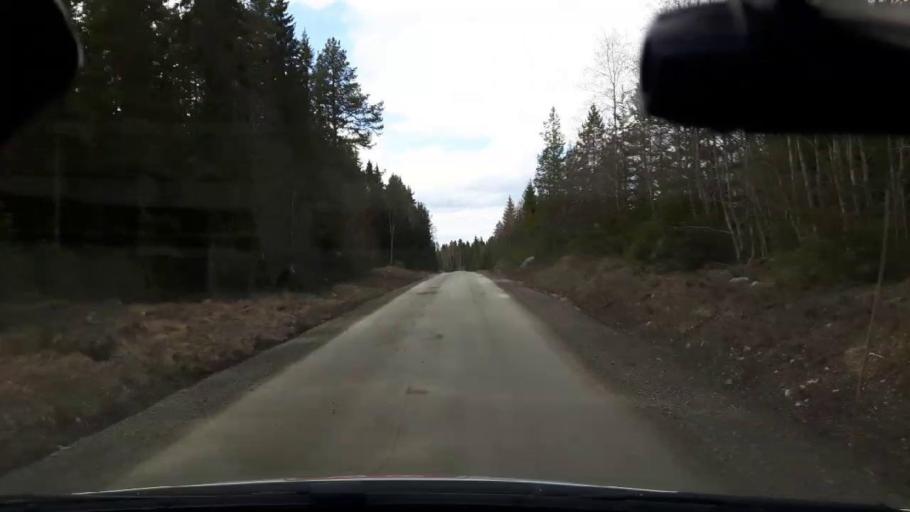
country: SE
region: Jaemtland
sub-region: Bergs Kommun
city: Hoverberg
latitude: 62.9037
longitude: 14.6395
